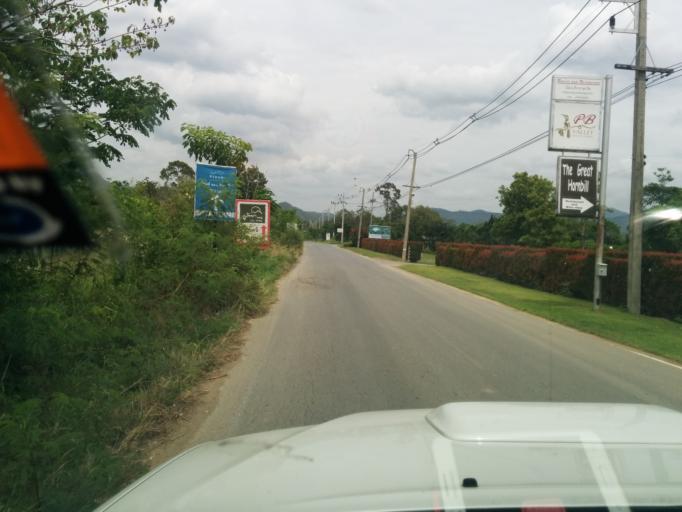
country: TH
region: Sara Buri
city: Muak Lek
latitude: 14.5768
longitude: 101.2347
